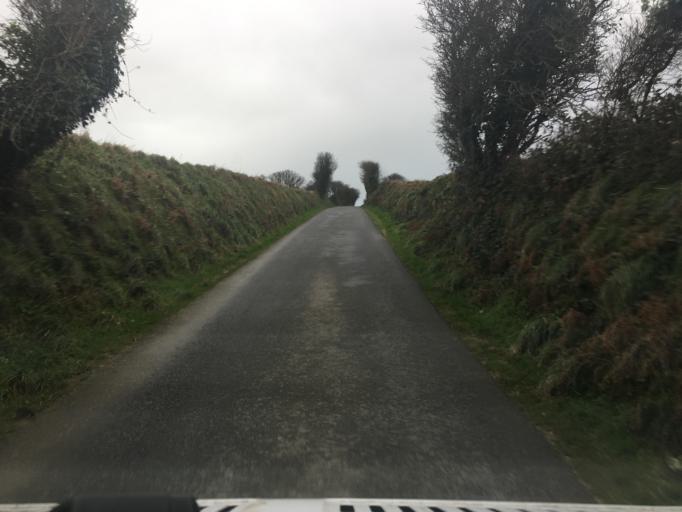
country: FR
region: Lower Normandy
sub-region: Departement de la Manche
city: Beaumont-Hague
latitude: 49.6851
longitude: -1.8679
